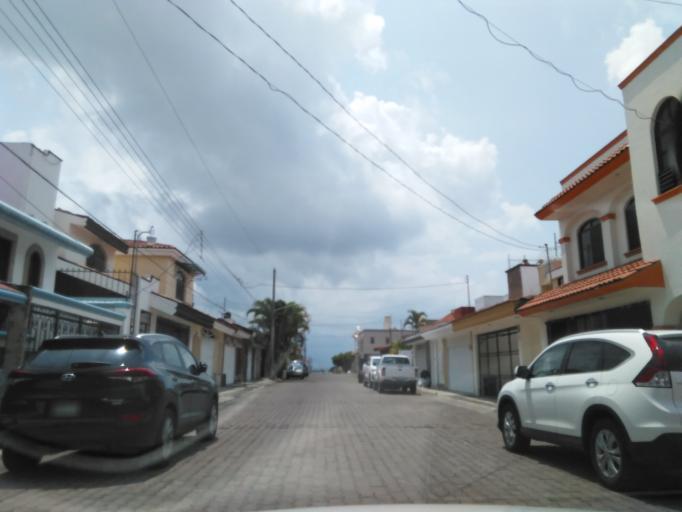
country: MX
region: Nayarit
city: Tepic
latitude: 21.5175
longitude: -104.9221
